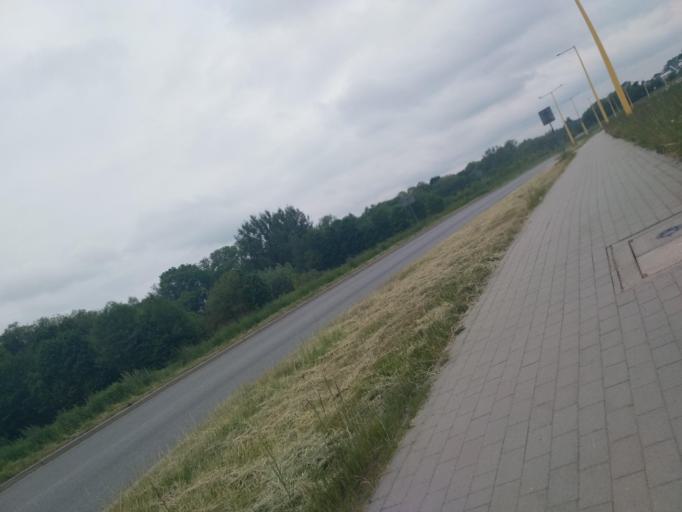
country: PL
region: Subcarpathian Voivodeship
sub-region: Krosno
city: Krosno
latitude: 49.6732
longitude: 21.7574
